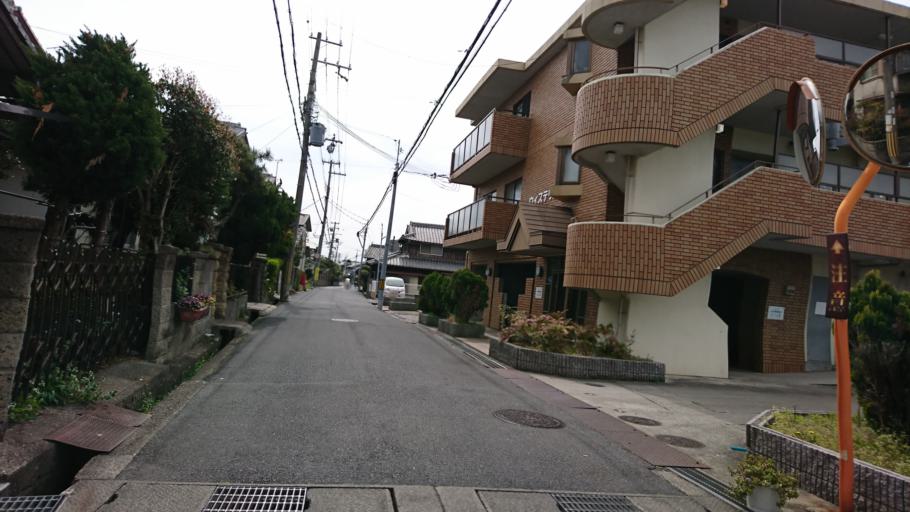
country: JP
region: Hyogo
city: Kakogawacho-honmachi
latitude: 34.7299
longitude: 134.8847
